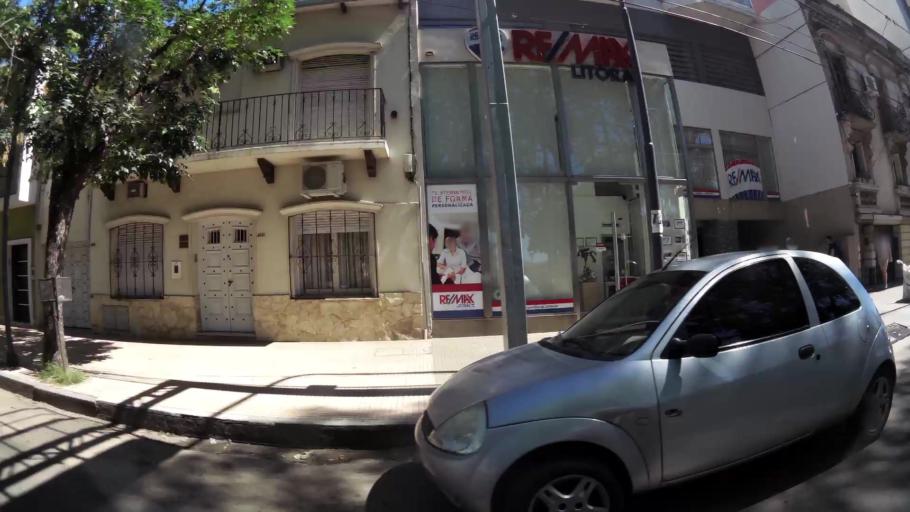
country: AR
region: Santa Fe
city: Santa Fe de la Vera Cruz
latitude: -31.6393
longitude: -60.6865
